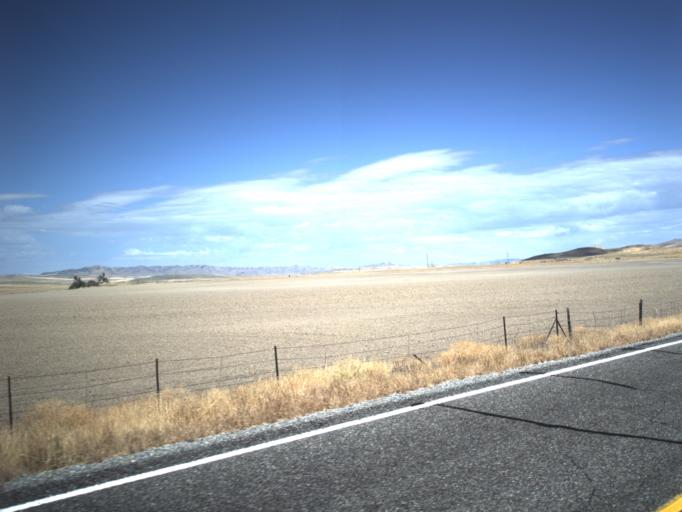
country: US
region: Utah
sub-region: Box Elder County
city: Garland
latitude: 41.8106
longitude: -112.4162
